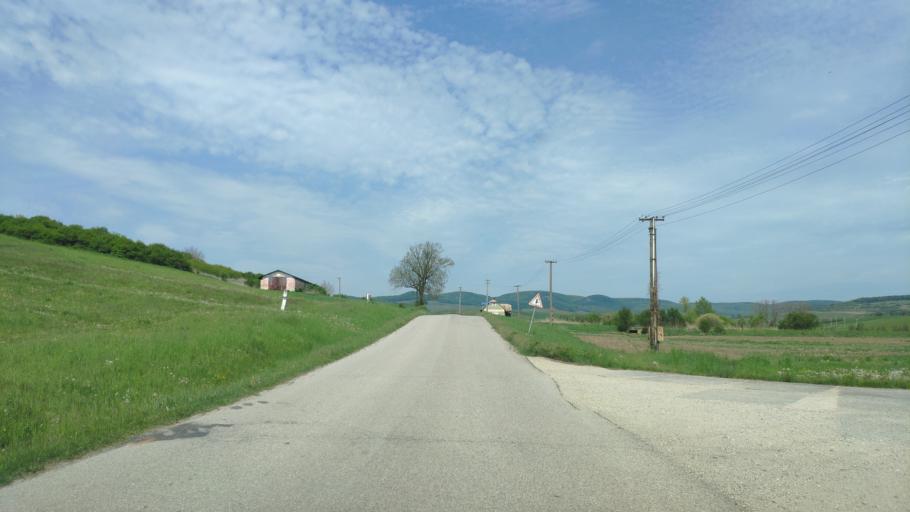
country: SK
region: Banskobystricky
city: Rimavska Sobota
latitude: 48.4234
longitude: 20.2199
